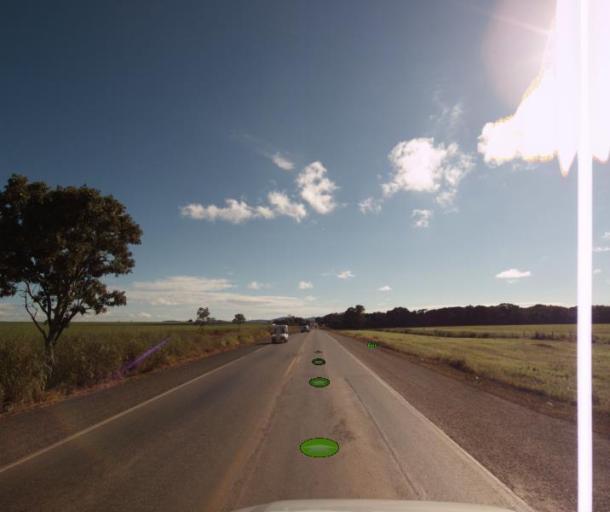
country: BR
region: Goias
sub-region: Uruacu
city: Uruacu
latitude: -14.6528
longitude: -49.1878
